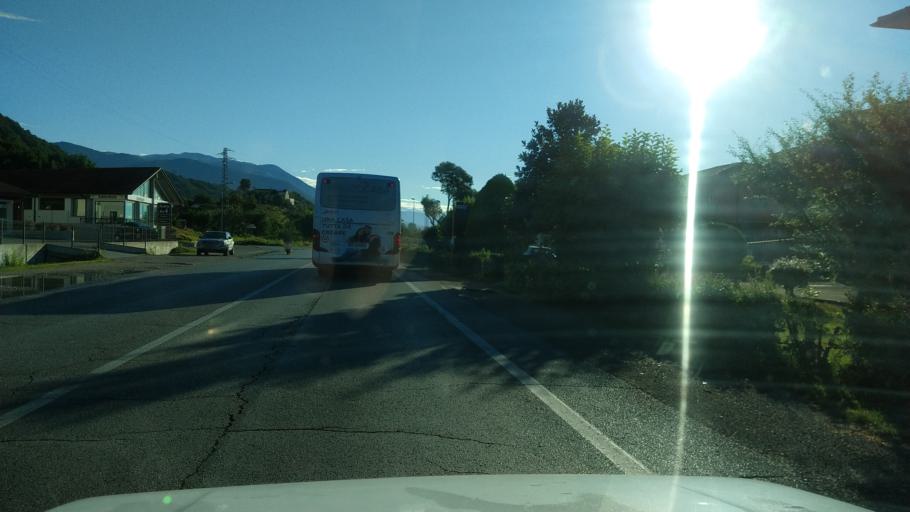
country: IT
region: Veneto
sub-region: Provincia di Vicenza
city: Marostica
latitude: 45.7593
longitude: 11.6878
